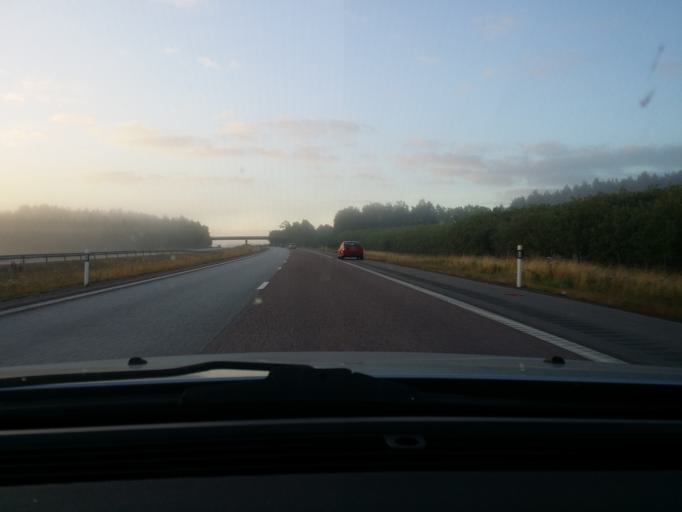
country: SE
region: Uppsala
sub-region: Habo Kommun
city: Balsta
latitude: 59.6017
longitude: 17.4378
